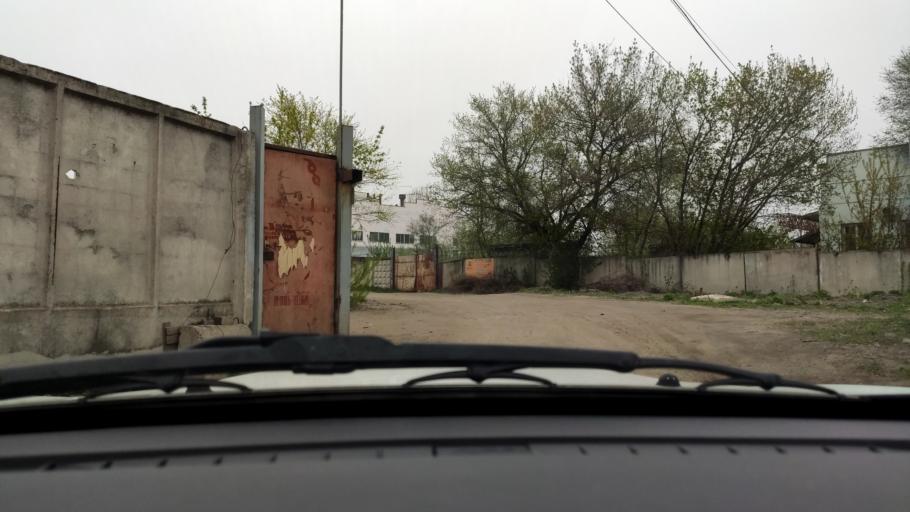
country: RU
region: Voronezj
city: Voronezh
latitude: 51.6416
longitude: 39.1323
